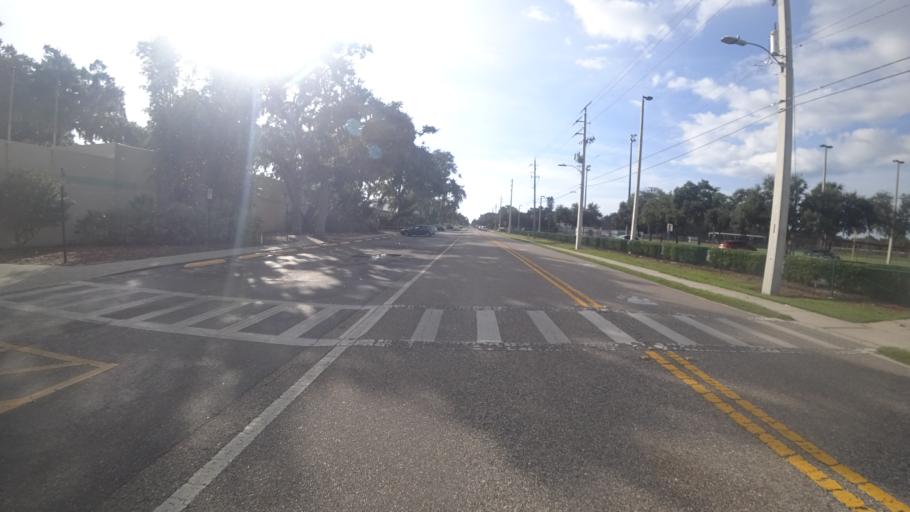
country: US
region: Florida
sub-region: Manatee County
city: Palmetto
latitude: 27.5286
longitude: -82.5794
